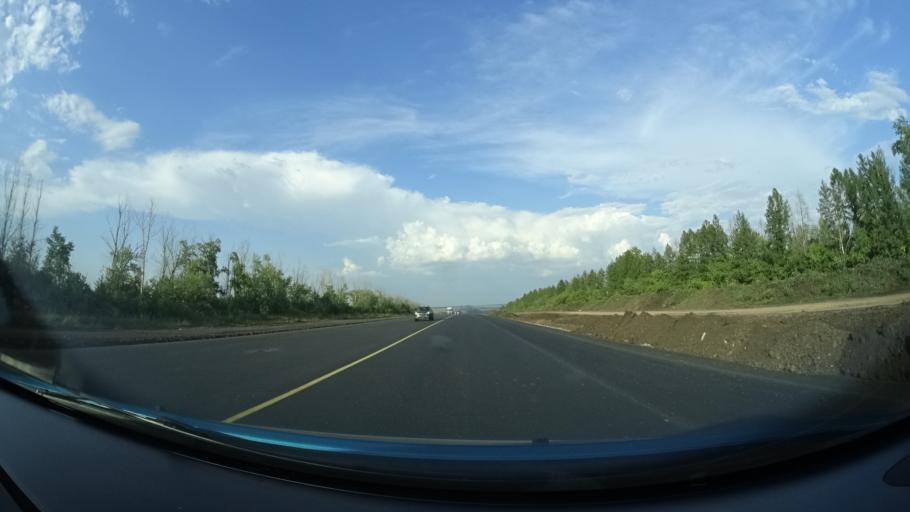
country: RU
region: Samara
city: Sukhodol
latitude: 53.7893
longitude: 50.9469
